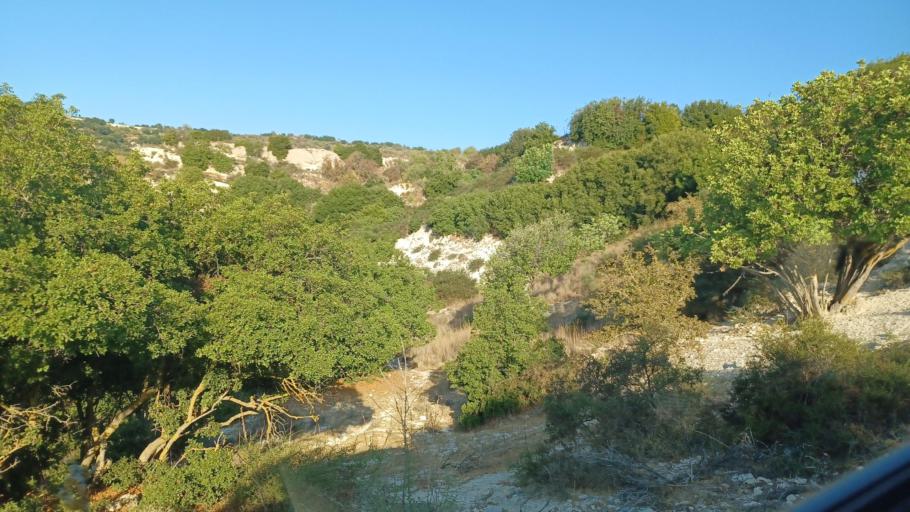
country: CY
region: Pafos
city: Mesogi
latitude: 34.8533
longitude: 32.5063
